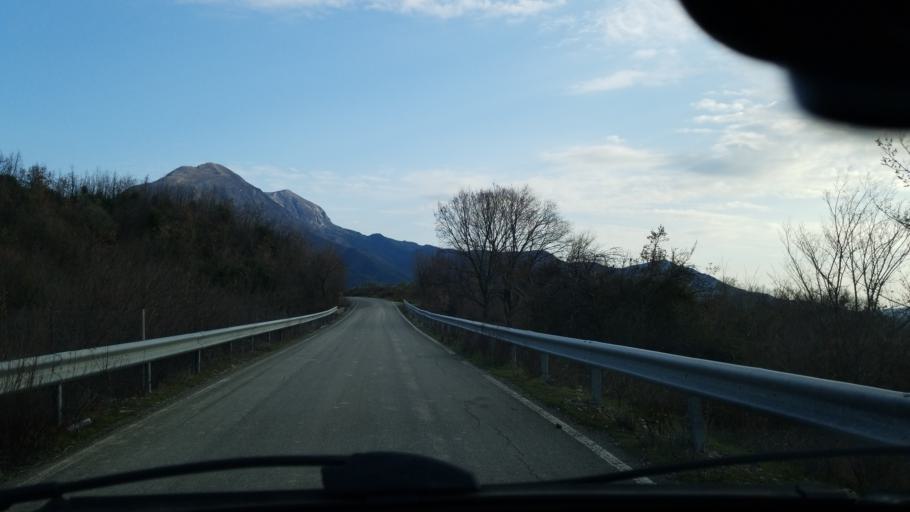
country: AL
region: Lezhe
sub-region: Rrethi i Lezhes
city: Kallmeti i Madh
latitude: 41.8797
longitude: 19.6924
